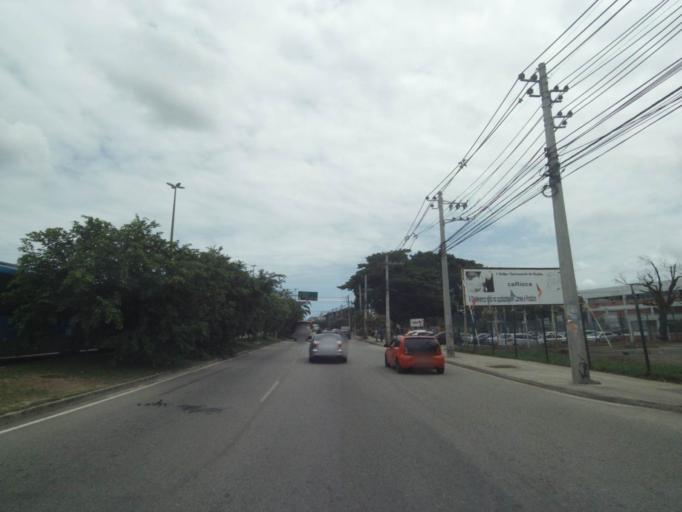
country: BR
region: Rio de Janeiro
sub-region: Sao Joao De Meriti
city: Sao Joao de Meriti
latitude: -22.9371
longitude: -43.3721
